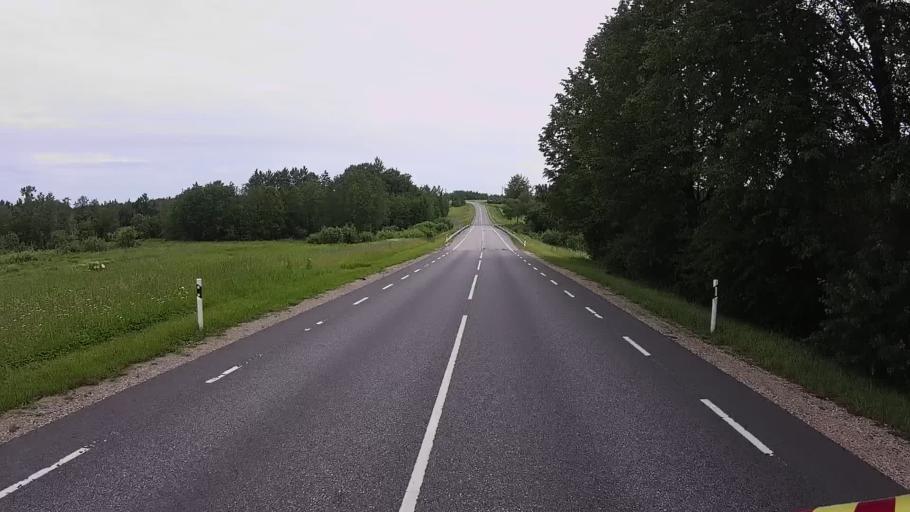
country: EE
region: Viljandimaa
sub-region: Karksi vald
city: Karksi-Nuia
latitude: 58.1460
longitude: 25.5915
